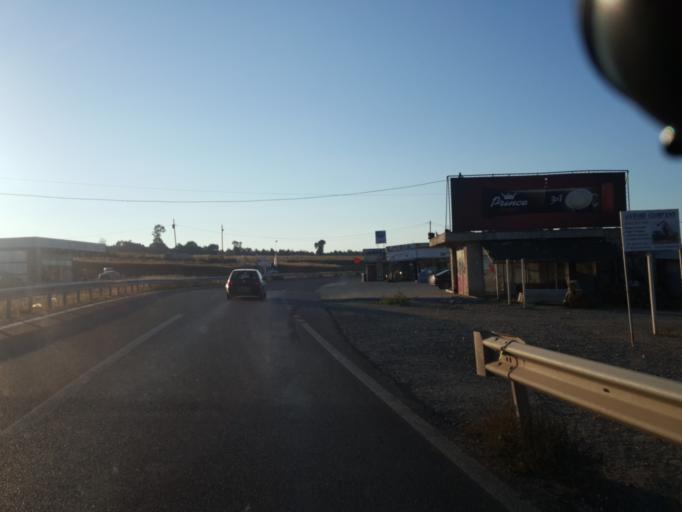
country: XK
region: Prizren
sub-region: Komuna e Malisheves
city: Llazice
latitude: 42.5644
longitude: 20.7712
